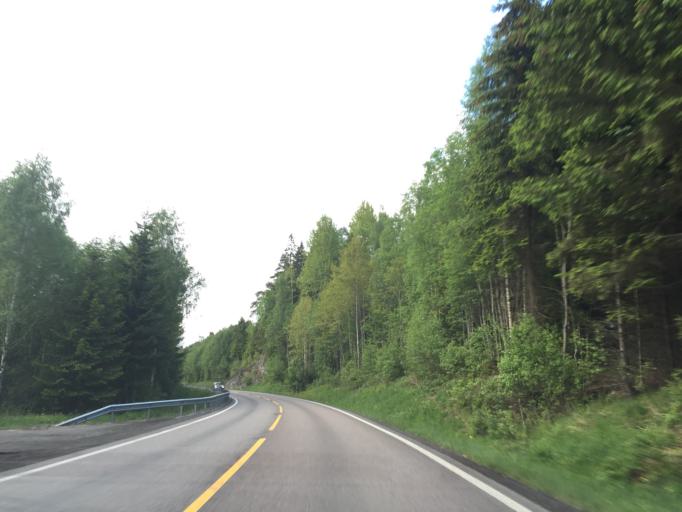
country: NO
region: Akershus
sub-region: Sorum
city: Sorumsand
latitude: 59.9511
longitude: 11.2028
